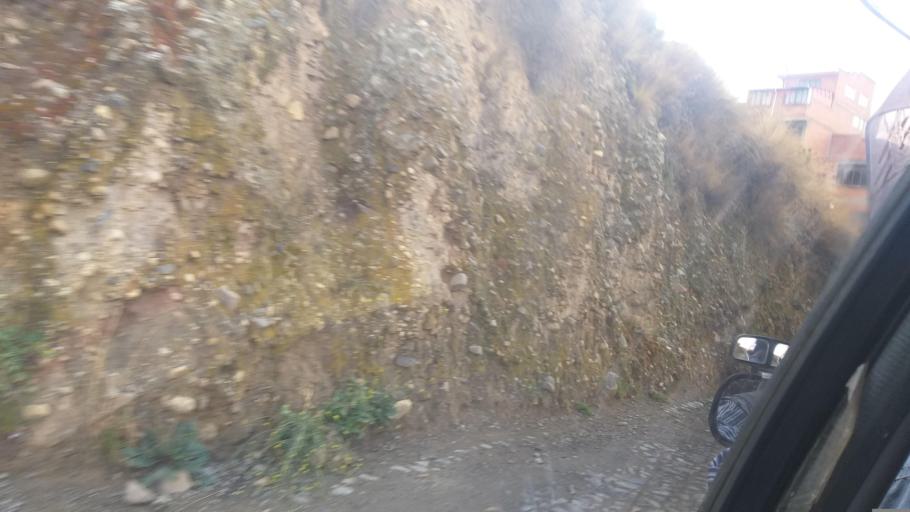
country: BO
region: La Paz
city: La Paz
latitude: -16.4672
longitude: -68.1486
